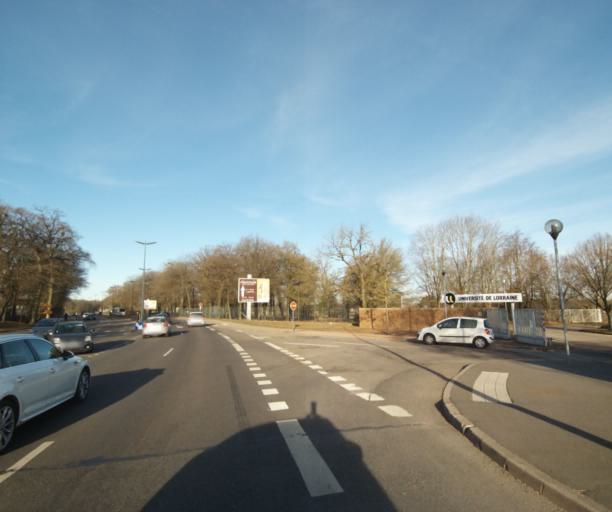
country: FR
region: Lorraine
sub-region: Departement de Meurthe-et-Moselle
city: Villers-les-Nancy
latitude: 48.6510
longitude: 6.1462
